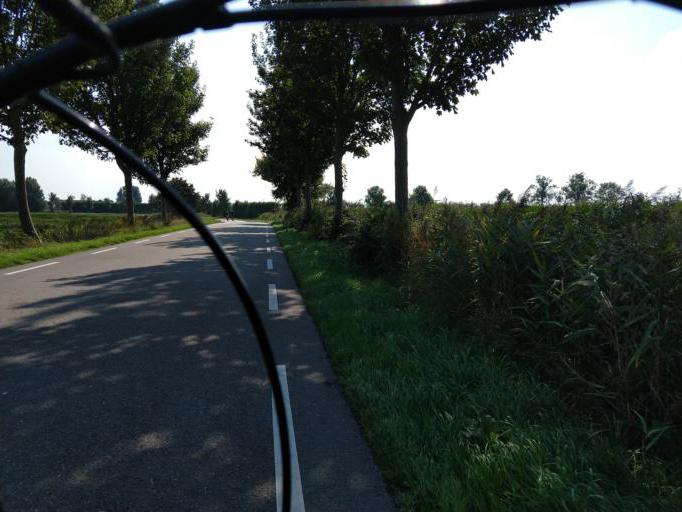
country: NL
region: Zeeland
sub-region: Gemeente Goes
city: Goes
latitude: 51.4192
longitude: 3.8798
